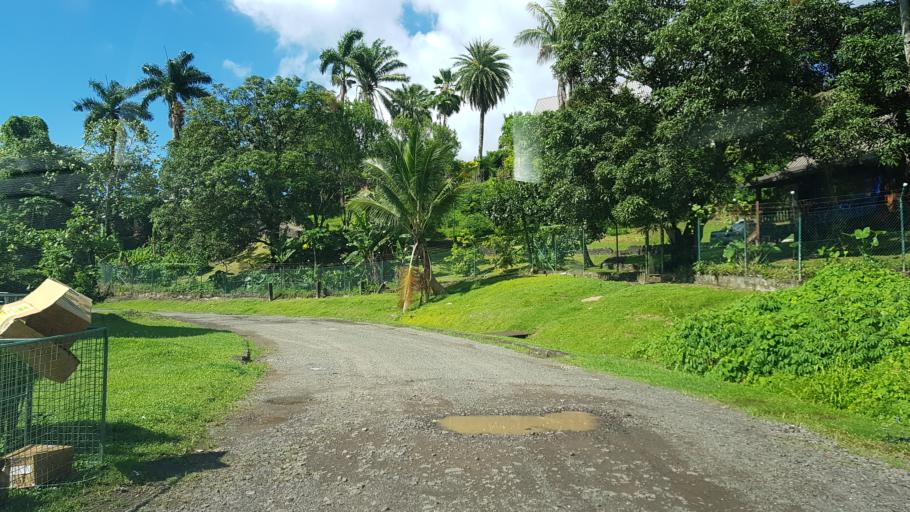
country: FJ
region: Central
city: Suva
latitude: -18.1489
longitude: 178.4407
